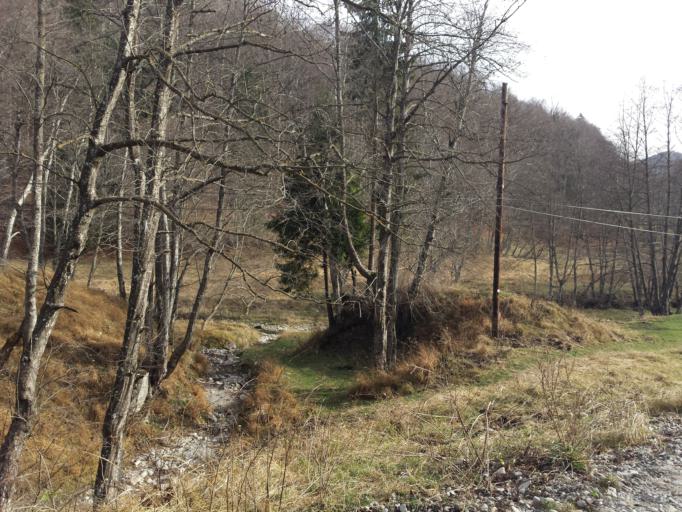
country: RO
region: Prahova
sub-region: Oras Azuga
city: Azuga
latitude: 45.4348
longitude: 25.5295
